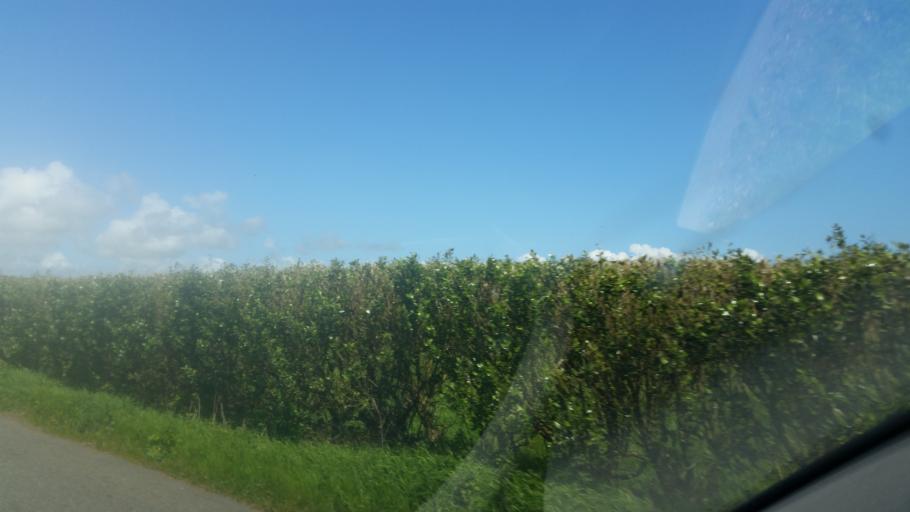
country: IE
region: Munster
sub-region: Waterford
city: Dunmore East
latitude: 52.1624
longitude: -6.8938
